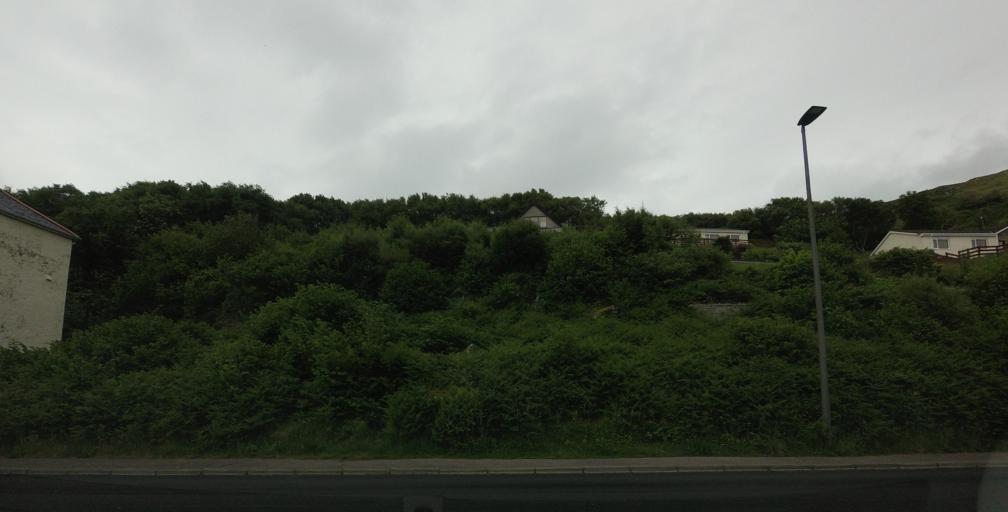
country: GB
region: Scotland
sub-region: Highland
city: Portree
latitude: 57.0052
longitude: -5.8223
